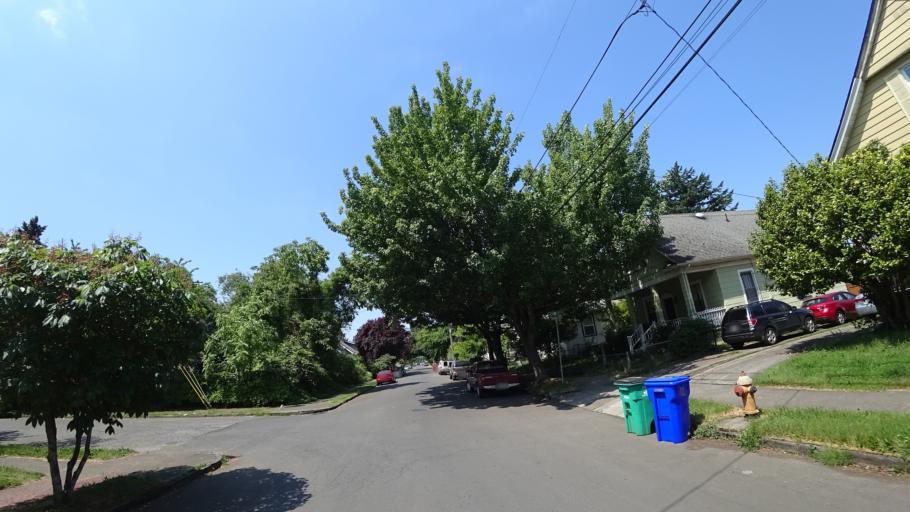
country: US
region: Oregon
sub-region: Multnomah County
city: Portland
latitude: 45.5600
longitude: -122.6534
